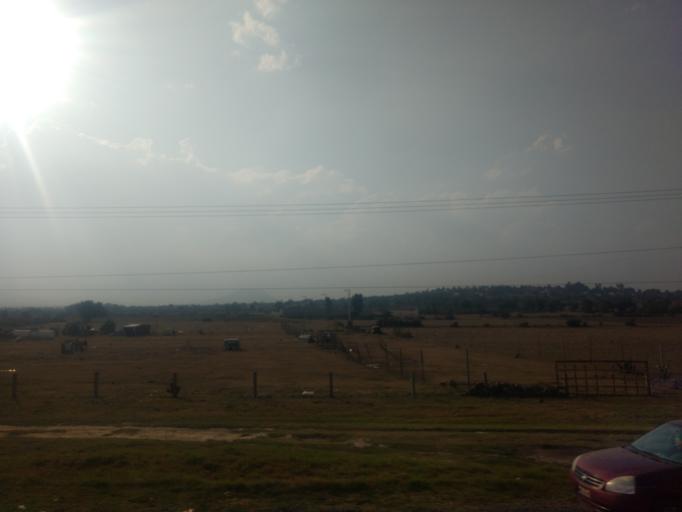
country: MX
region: Morelos
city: Nopaltepec
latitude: 19.7696
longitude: -98.7444
